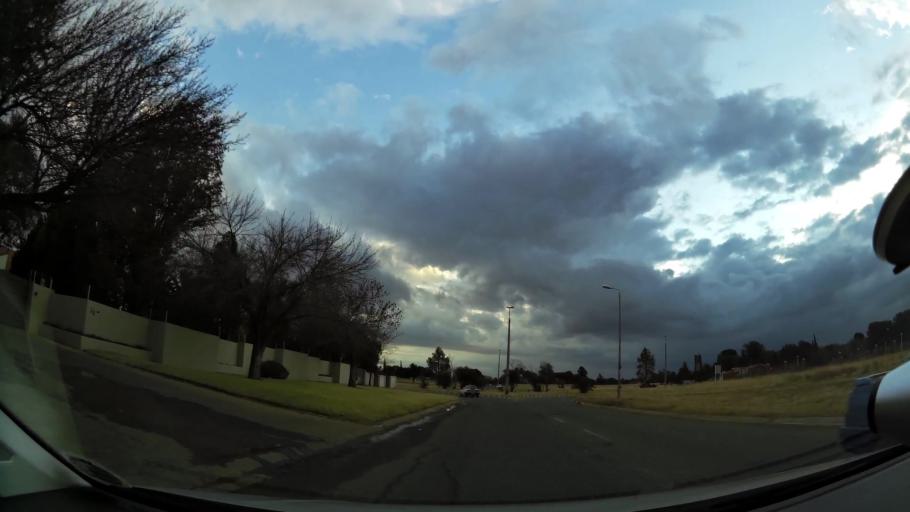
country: ZA
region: Orange Free State
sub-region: Lejweleputswa District Municipality
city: Welkom
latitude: -27.9554
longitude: 26.7363
